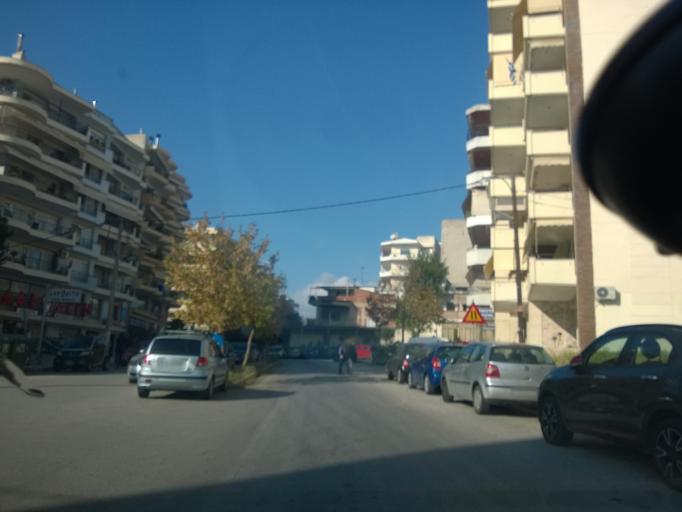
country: GR
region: Central Macedonia
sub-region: Nomos Thessalonikis
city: Stavroupoli
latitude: 40.6708
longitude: 22.9243
